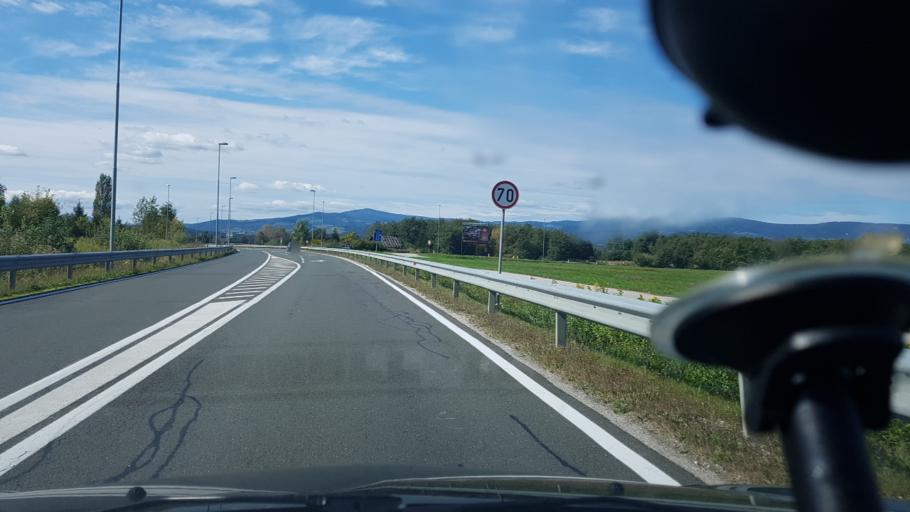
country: SI
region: Slovenska Bistrica
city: Pragersko
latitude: 46.4116
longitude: 15.6871
